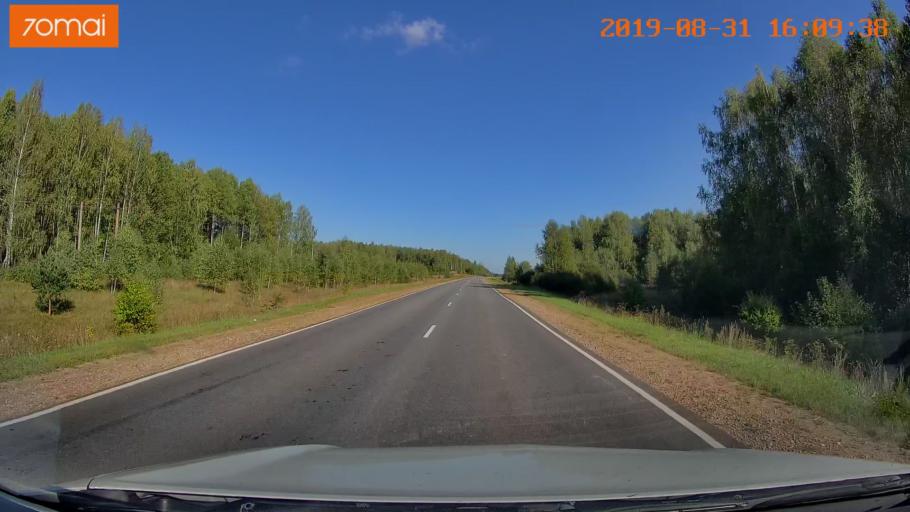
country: RU
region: Kaluga
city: Yukhnov
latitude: 54.5878
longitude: 35.4042
